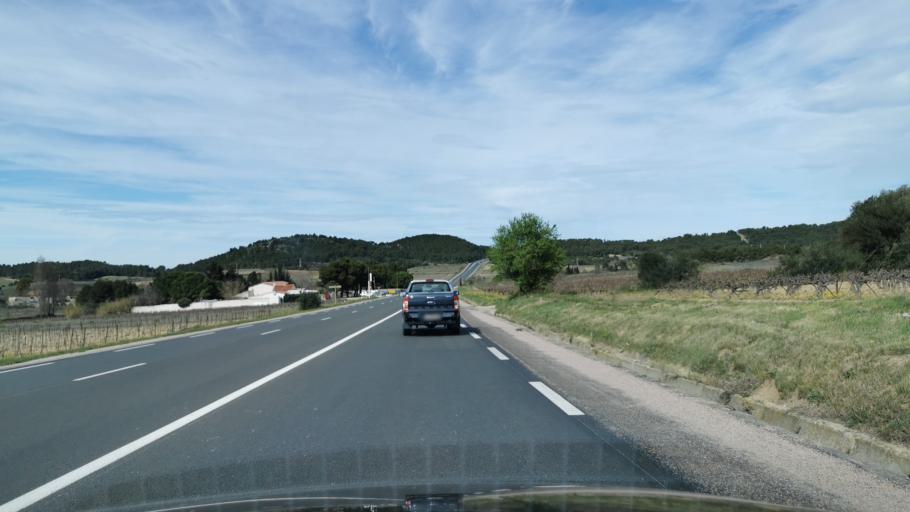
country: FR
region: Languedoc-Roussillon
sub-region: Departement de l'Aude
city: Sigean
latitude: 42.9976
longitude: 2.9700
